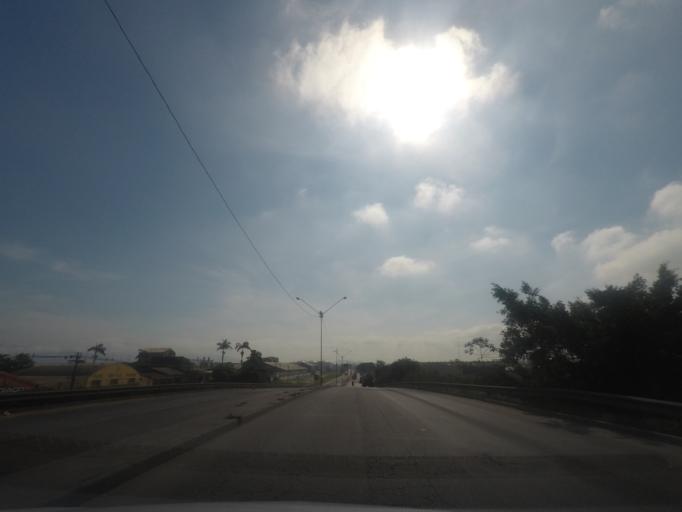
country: BR
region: Parana
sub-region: Paranagua
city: Paranagua
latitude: -25.5253
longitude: -48.5269
